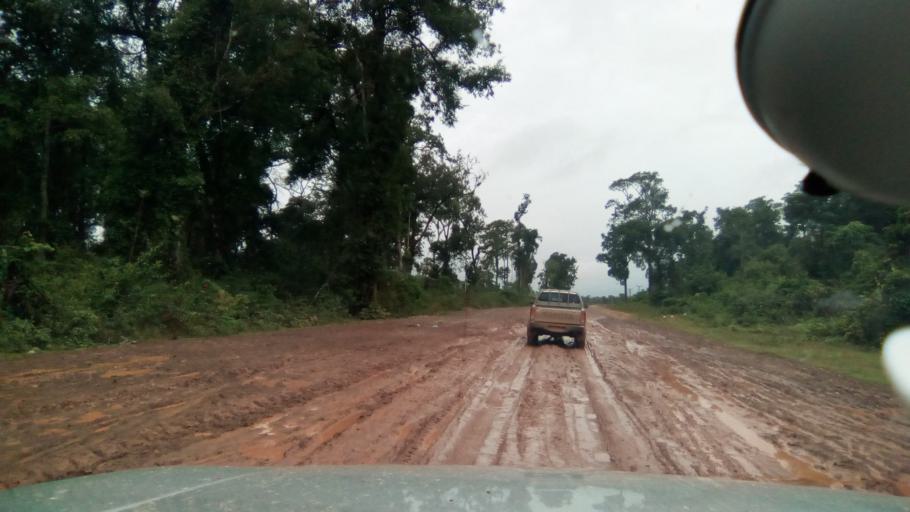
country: LA
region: Attapu
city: Attapu
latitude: 14.6846
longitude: 106.5505
